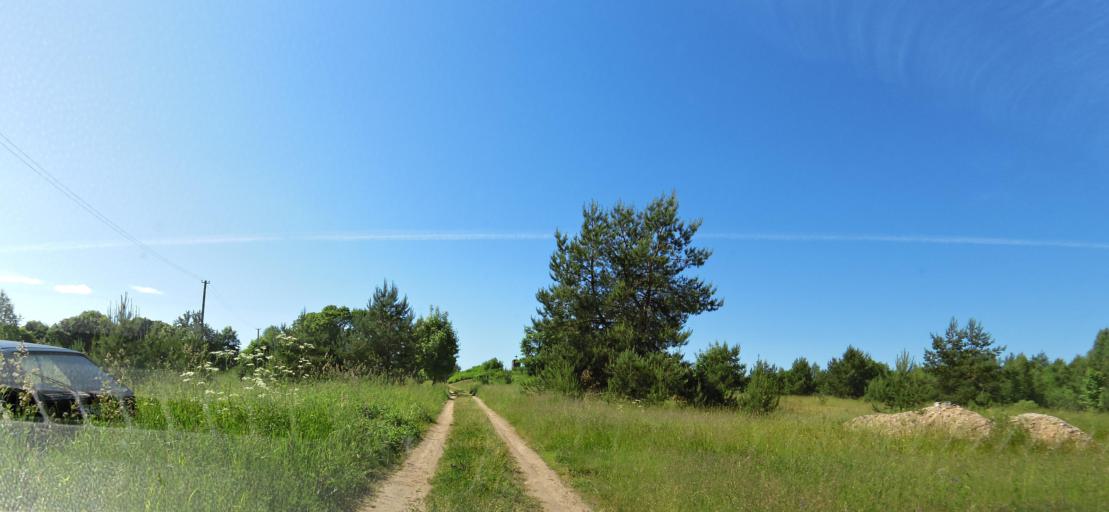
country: LT
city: Sirvintos
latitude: 55.2566
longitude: 25.1026
